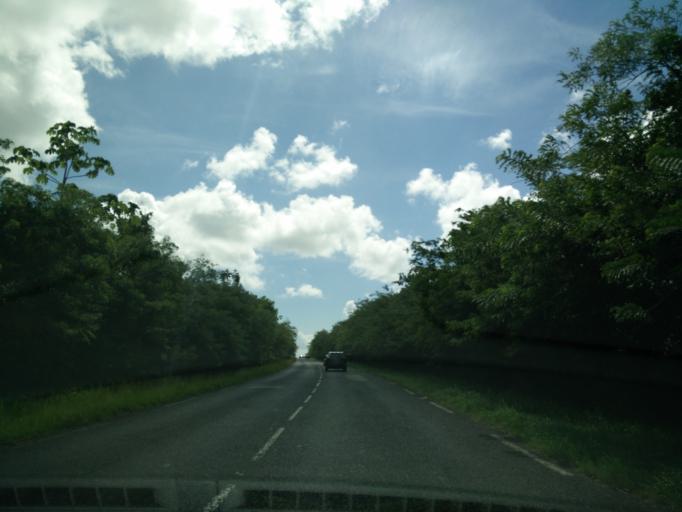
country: MQ
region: Martinique
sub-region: Martinique
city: Les Trois-Ilets
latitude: 14.5274
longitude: -60.9927
